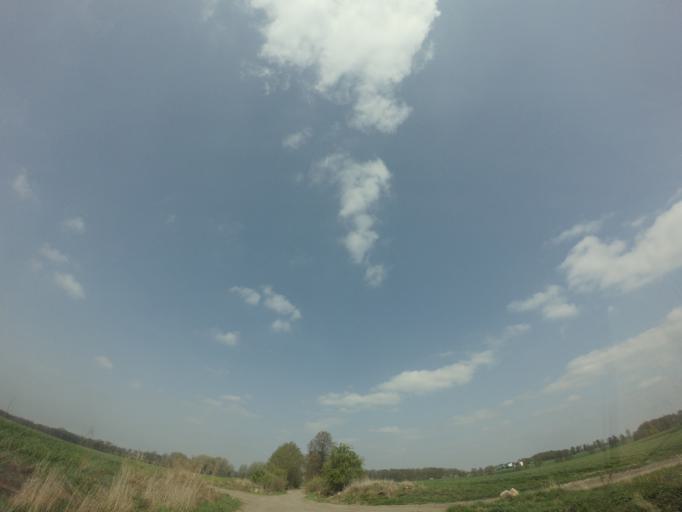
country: PL
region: West Pomeranian Voivodeship
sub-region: Powiat choszczenski
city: Pelczyce
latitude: 53.0887
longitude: 15.3431
